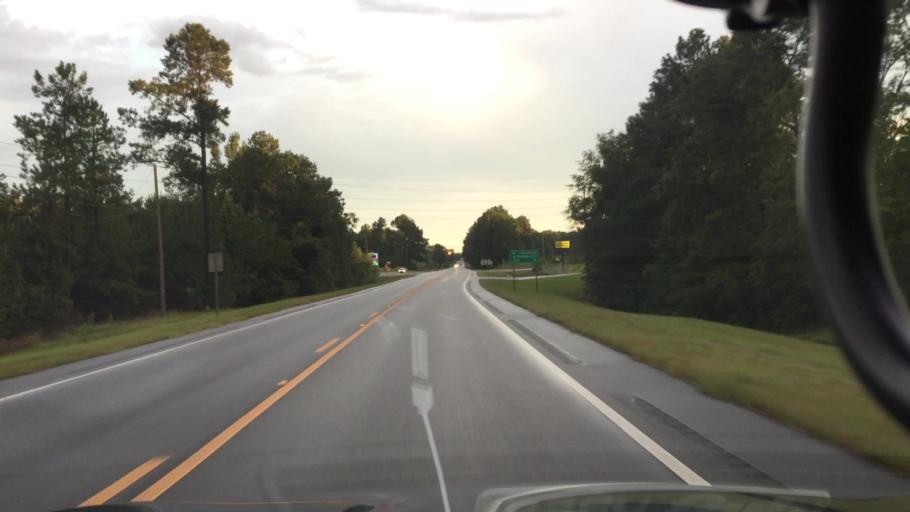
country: US
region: Alabama
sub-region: Coffee County
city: New Brockton
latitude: 31.5453
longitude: -85.9190
